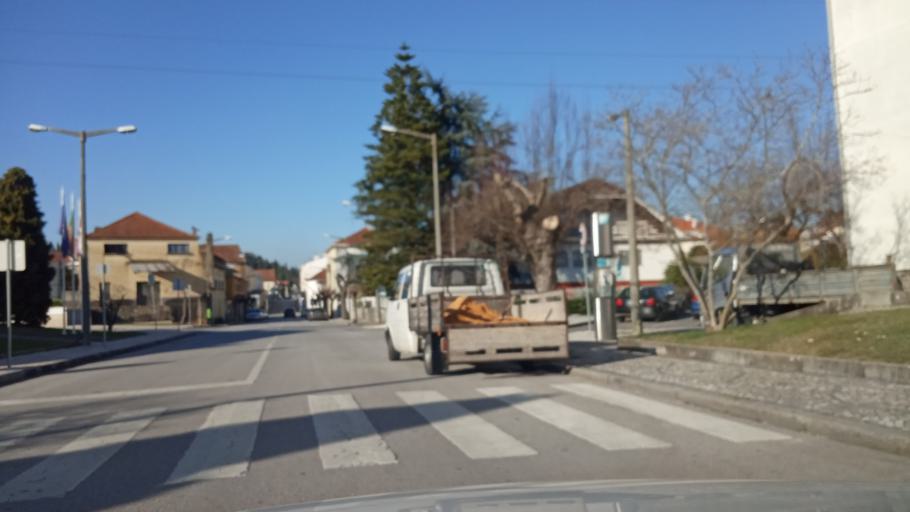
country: PT
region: Aveiro
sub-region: Anadia
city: Anadia
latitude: 40.4387
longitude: -8.4353
